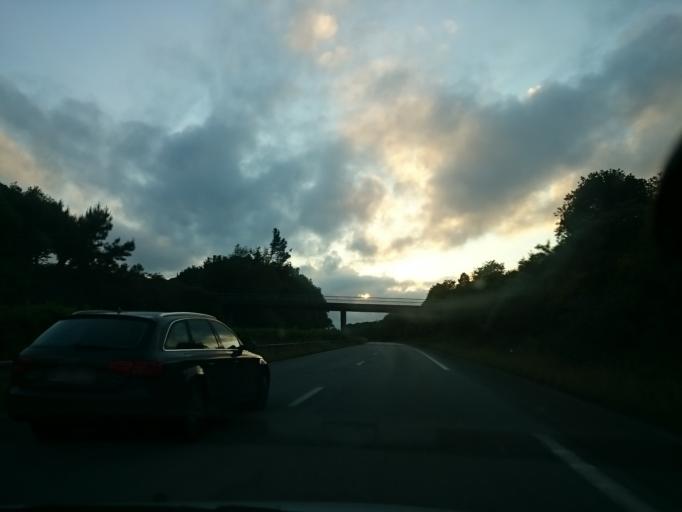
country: FR
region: Brittany
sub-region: Departement du Morbihan
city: Queven
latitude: 47.7875
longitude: -3.4339
